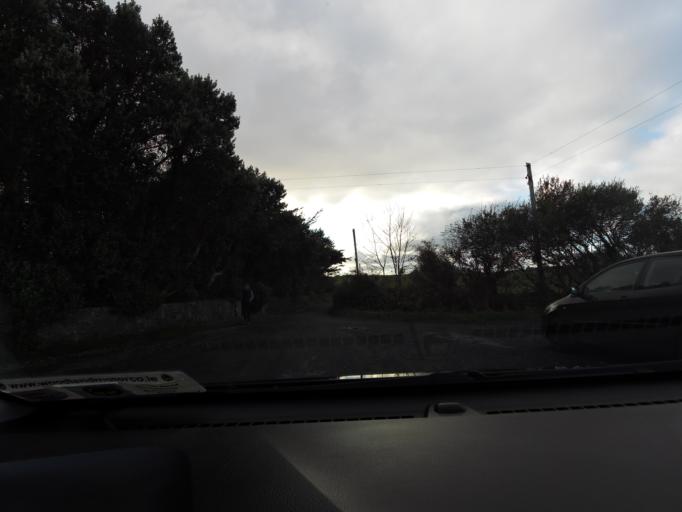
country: IE
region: Connaught
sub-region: Maigh Eo
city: Belmullet
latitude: 53.9969
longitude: -9.9300
